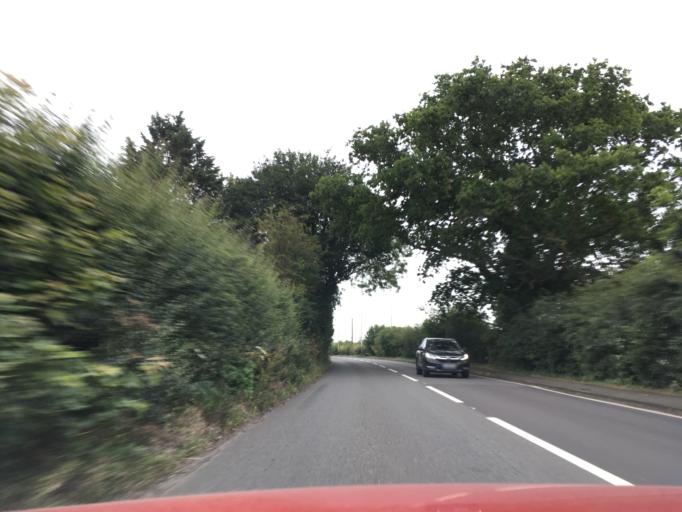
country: GB
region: England
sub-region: Hertfordshire
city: Flamstead
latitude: 51.8249
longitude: -0.4356
